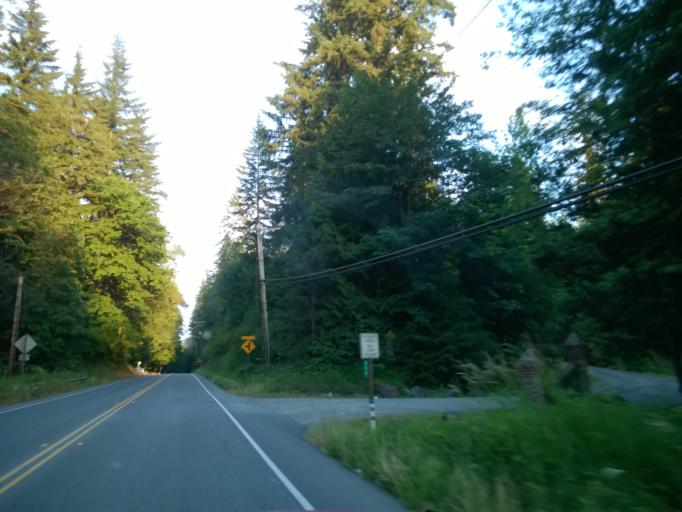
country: US
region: Washington
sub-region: King County
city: Duvall
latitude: 47.7561
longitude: -122.0245
